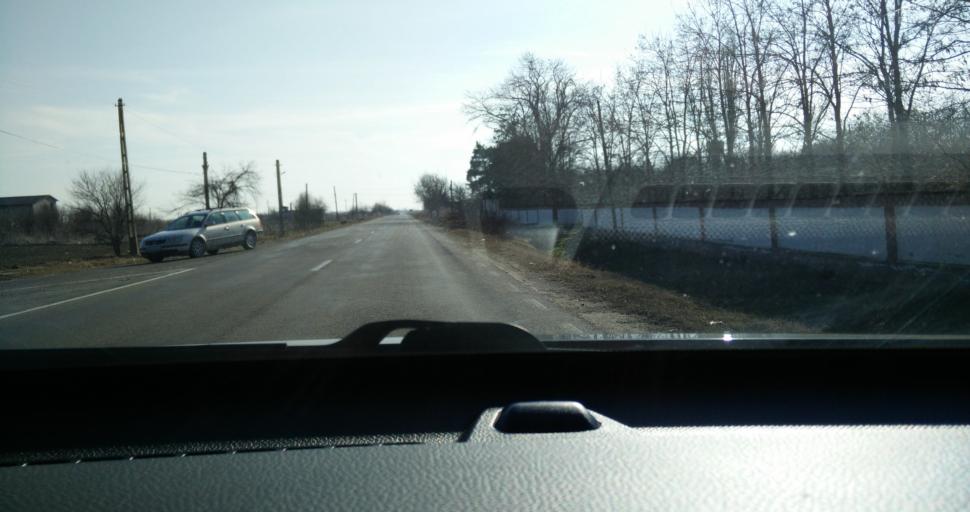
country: RO
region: Vrancea
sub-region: Comuna Nanesti
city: Nanesti
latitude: 45.5278
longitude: 27.4951
